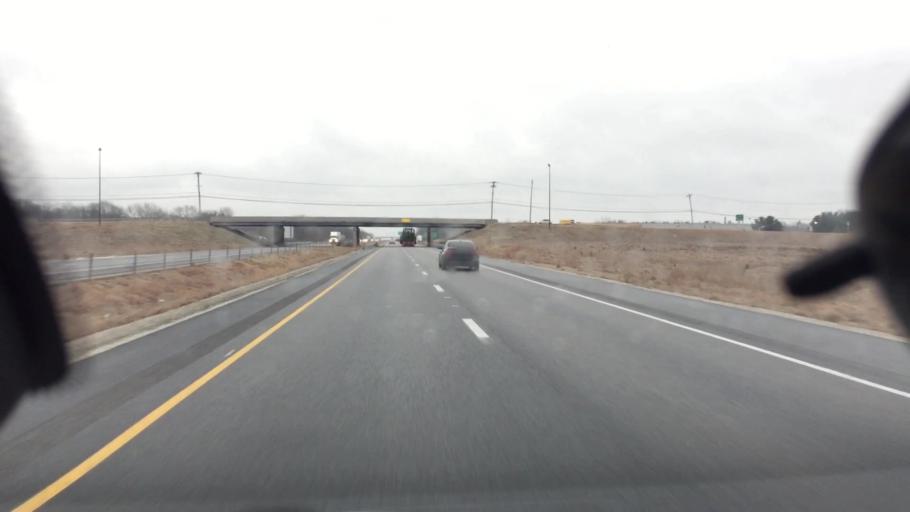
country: US
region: Illinois
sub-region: Tazewell County
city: East Peoria
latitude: 40.6440
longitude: -89.5425
